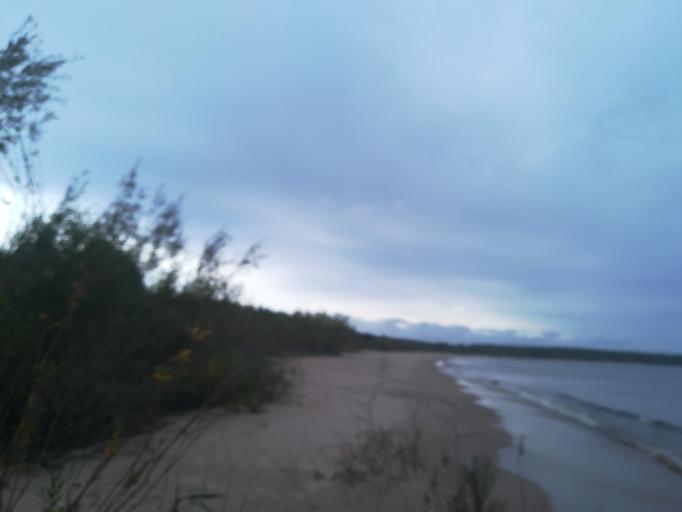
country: RU
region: Leningrad
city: Priozersk
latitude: 61.0408
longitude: 30.1915
